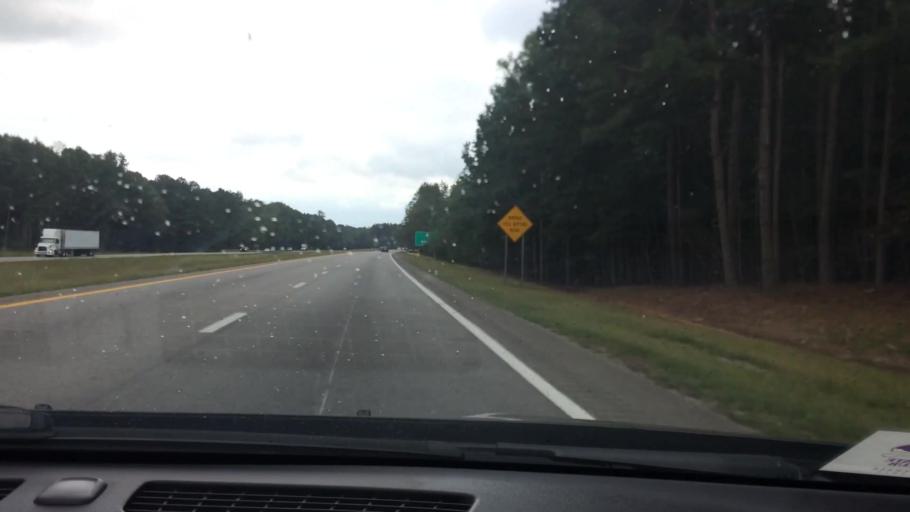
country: US
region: North Carolina
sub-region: Wake County
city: Zebulon
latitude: 35.8065
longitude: -78.2110
